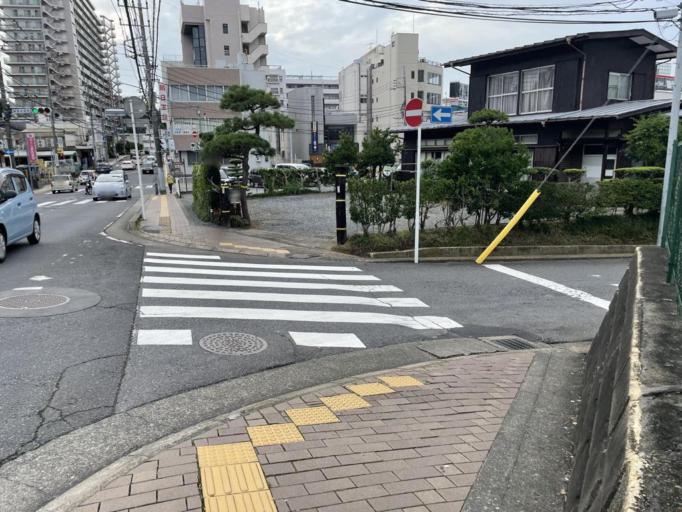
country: JP
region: Chiba
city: Sakura
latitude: 35.7240
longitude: 140.2307
